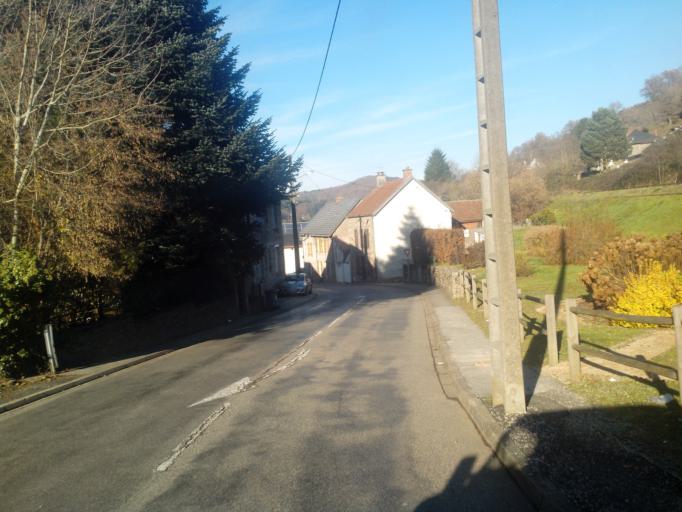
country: FR
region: Limousin
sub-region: Departement de la Correze
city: Bort-les-Orgues
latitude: 45.3977
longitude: 2.4995
